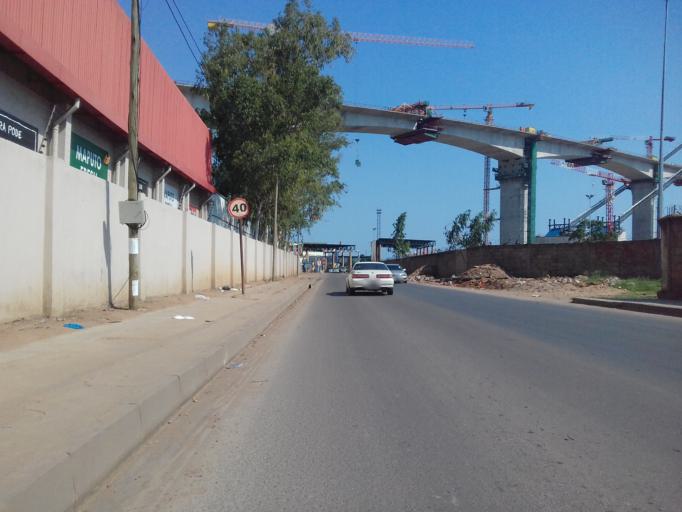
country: MZ
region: Maputo City
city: Maputo
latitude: -25.9647
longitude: 32.5587
